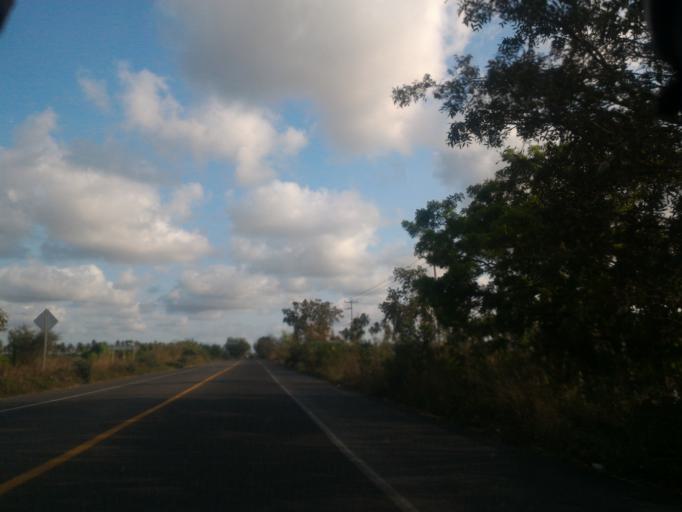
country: MX
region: Colima
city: Tecoman
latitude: 18.8469
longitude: -103.8265
